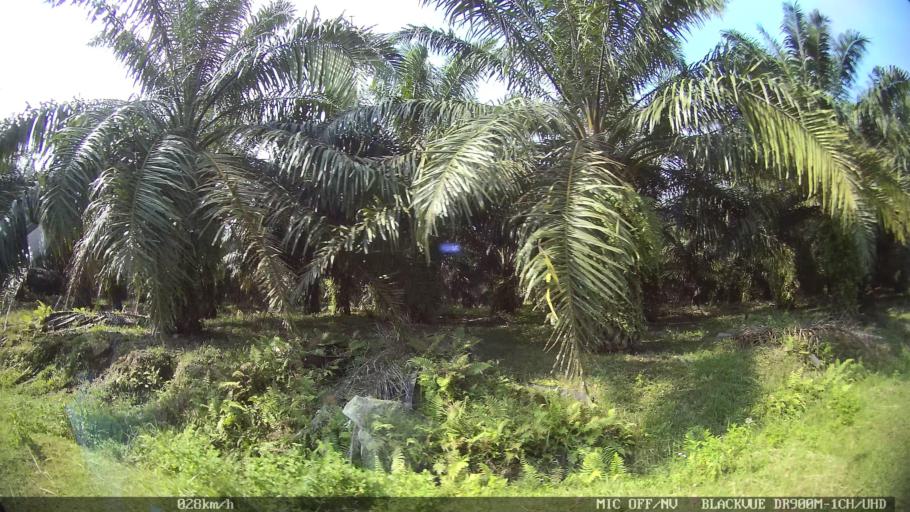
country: ID
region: North Sumatra
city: Binjai
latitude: 3.6426
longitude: 98.5277
